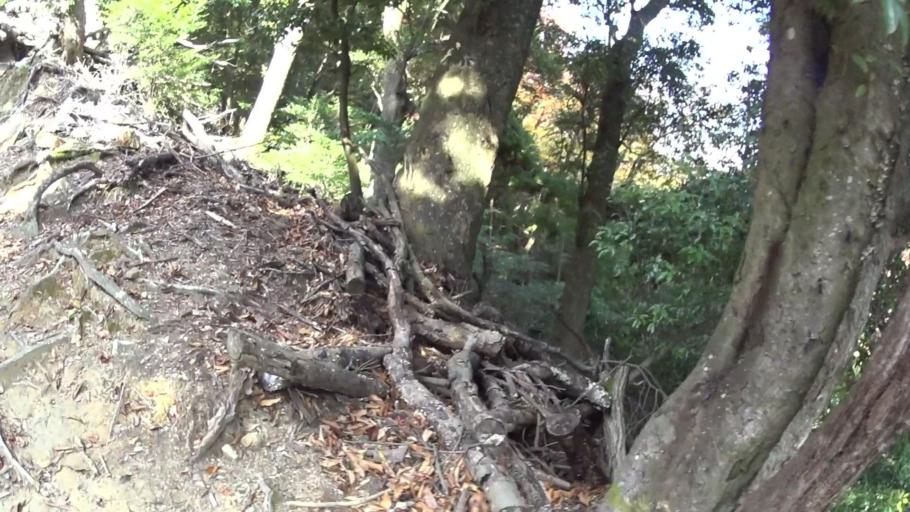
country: JP
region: Kyoto
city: Kameoka
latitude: 35.0469
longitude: 135.6467
